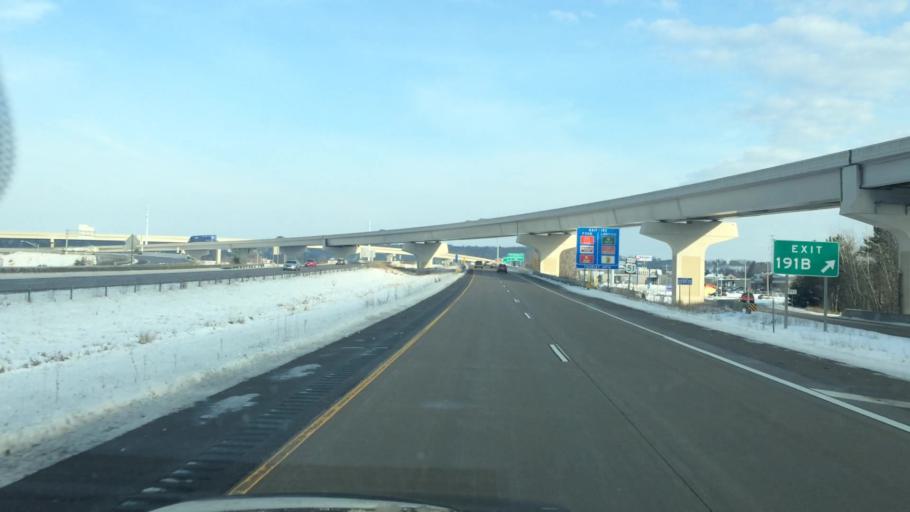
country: US
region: Wisconsin
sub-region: Marathon County
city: Wausau
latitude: 44.9497
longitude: -89.6665
